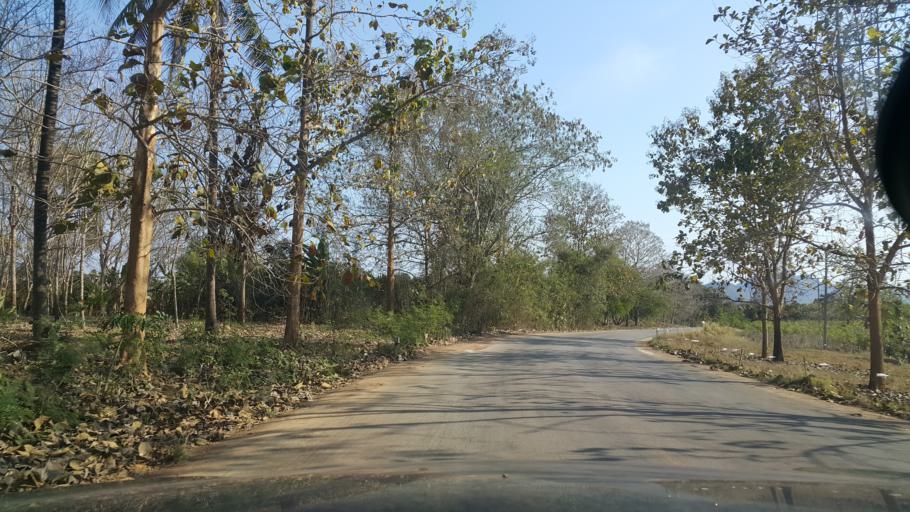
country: TH
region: Loei
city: Chiang Khan
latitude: 17.8490
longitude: 101.6446
